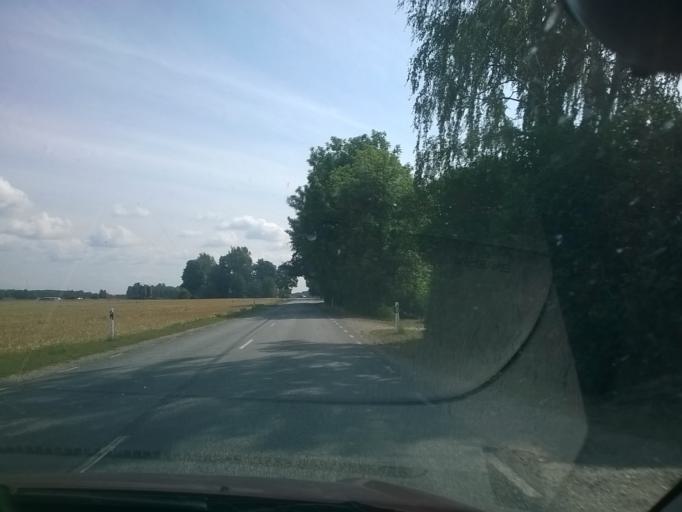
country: EE
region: Tartu
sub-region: Puhja vald
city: Puhja
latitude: 58.2555
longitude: 26.1798
